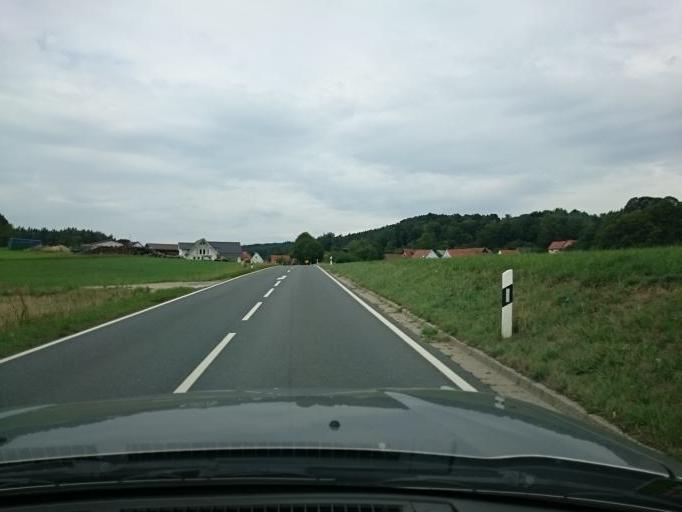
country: DE
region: Bavaria
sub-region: Regierungsbezirk Mittelfranken
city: Velden
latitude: 49.6402
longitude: 11.5149
